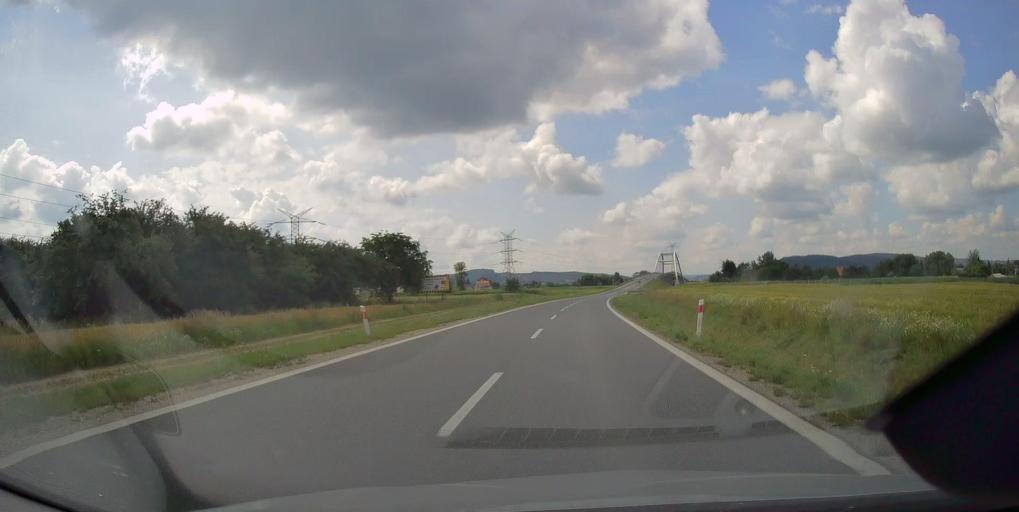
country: PL
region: Lesser Poland Voivodeship
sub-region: Powiat tarnowski
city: Wojnicz
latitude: 49.9553
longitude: 20.8523
